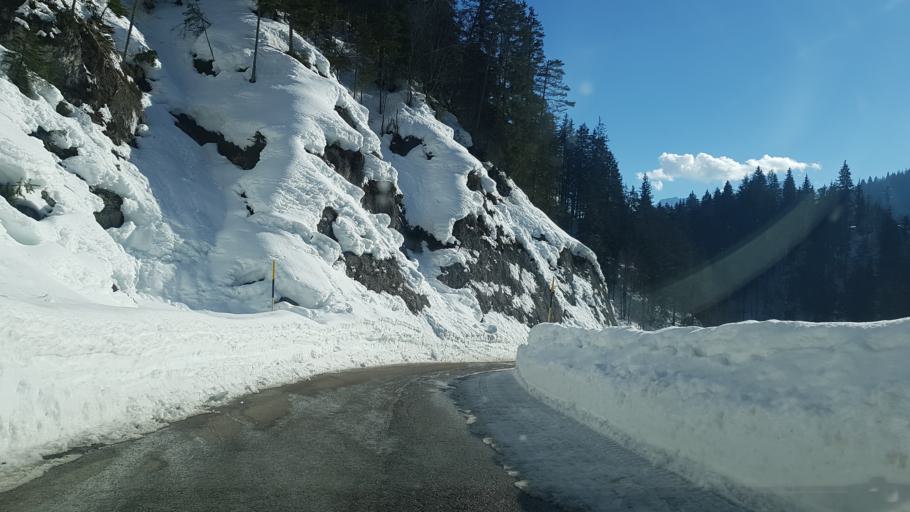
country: IT
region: Friuli Venezia Giulia
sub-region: Provincia di Udine
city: Malborghetto
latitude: 46.5332
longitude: 13.4712
